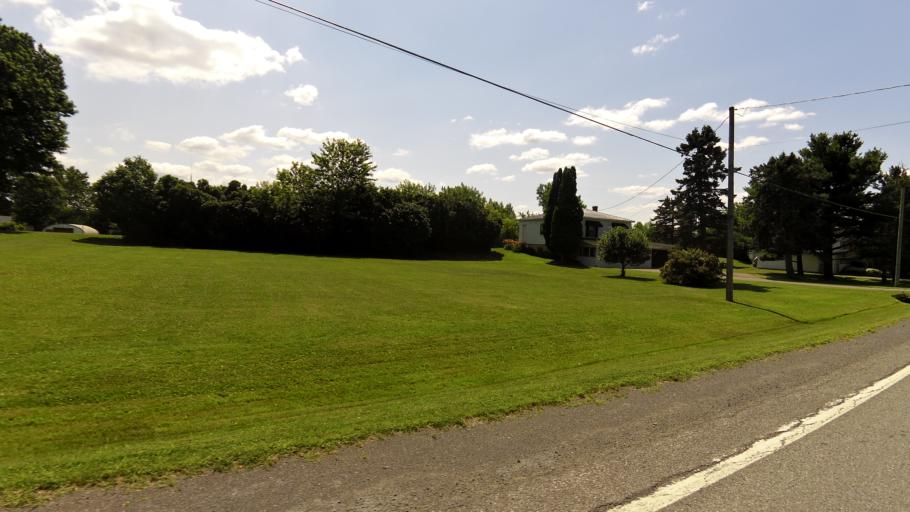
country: CA
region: Quebec
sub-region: Monteregie
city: Richelieu
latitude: 45.4079
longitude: -73.2555
